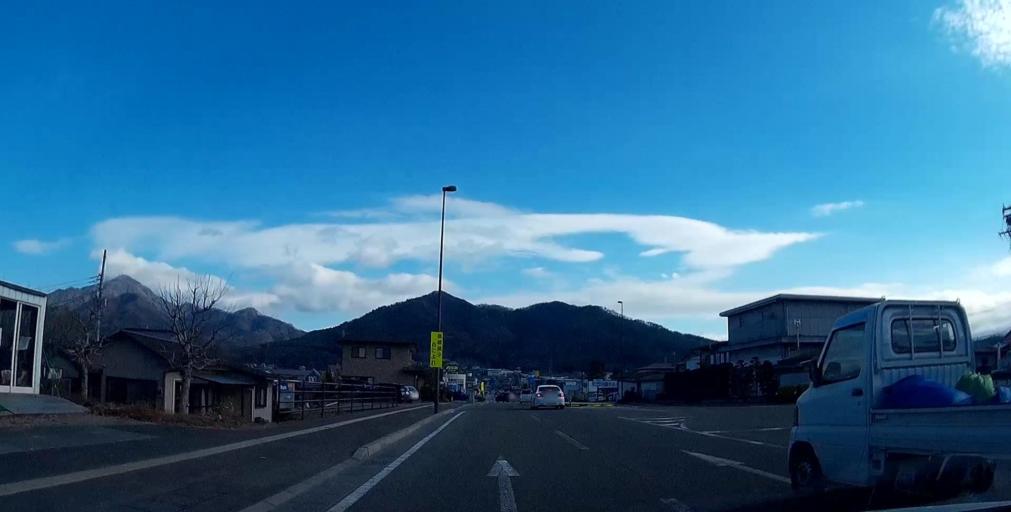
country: JP
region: Yamanashi
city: Fujikawaguchiko
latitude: 35.4834
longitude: 138.8065
